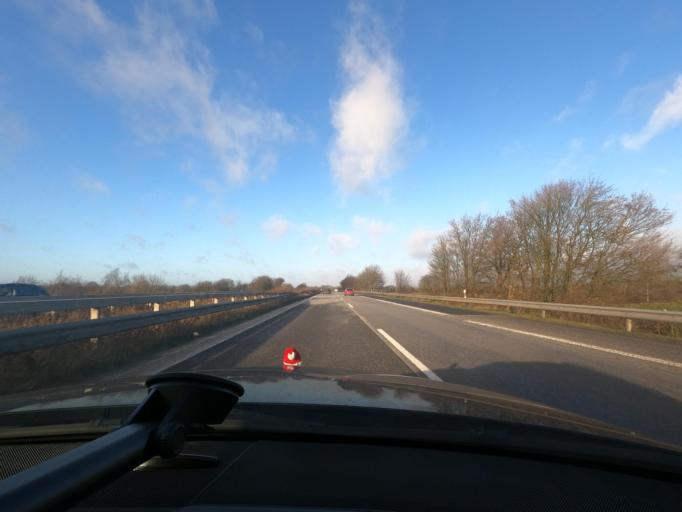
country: DE
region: Schleswig-Holstein
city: Lottorf
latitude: 54.4478
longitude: 9.5864
